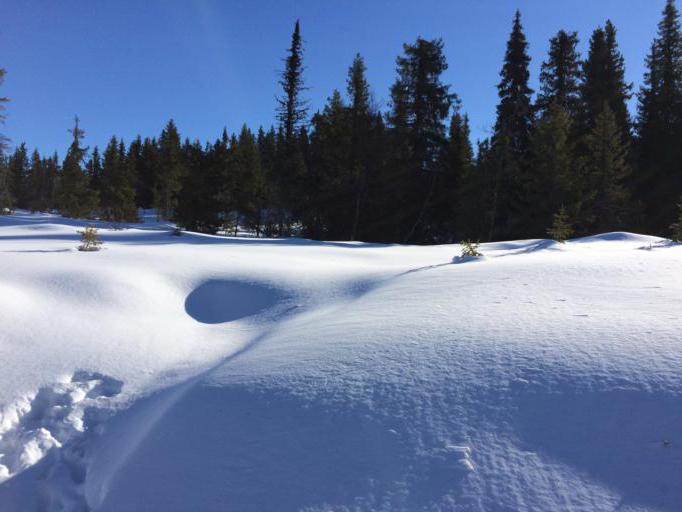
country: NO
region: Oppland
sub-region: Gausdal
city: Segalstad bru
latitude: 61.3185
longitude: 10.0787
